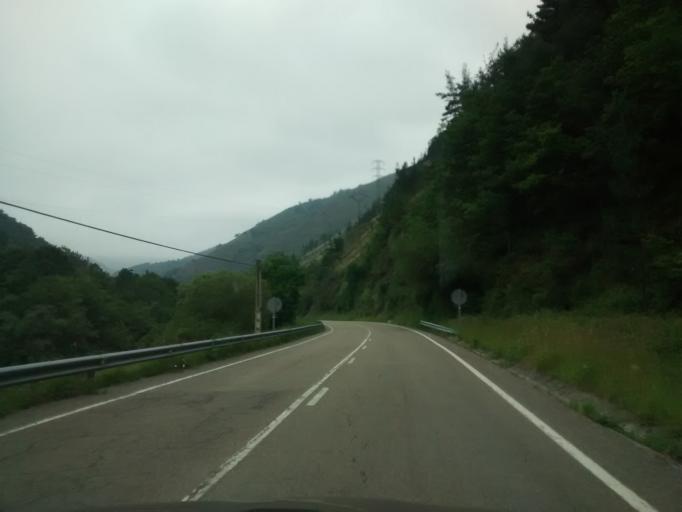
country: ES
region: Cantabria
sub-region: Provincia de Cantabria
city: Ruente
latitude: 43.1611
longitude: -4.2522
